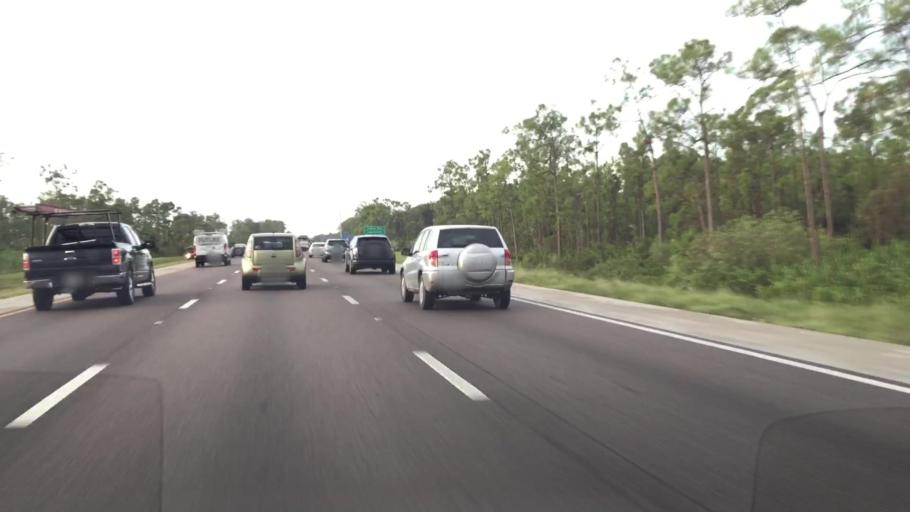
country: US
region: Florida
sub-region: Lee County
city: Gateway
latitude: 26.5662
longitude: -81.7941
